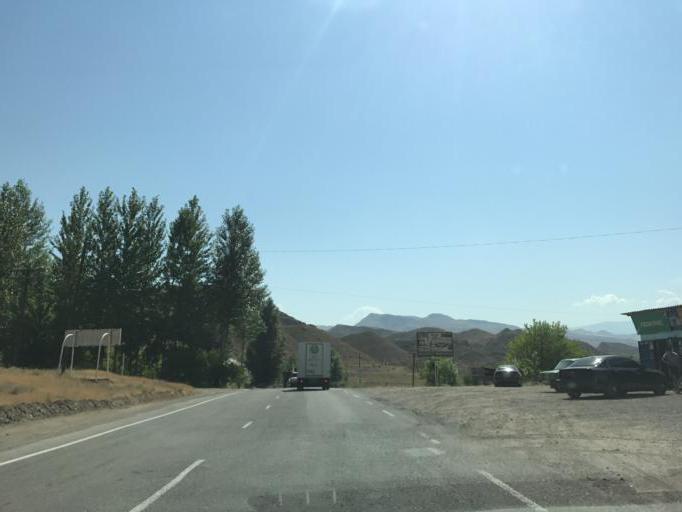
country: AM
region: Vayots' Dzori Marz
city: Yeghegnadzor
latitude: 39.7575
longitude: 45.3467
